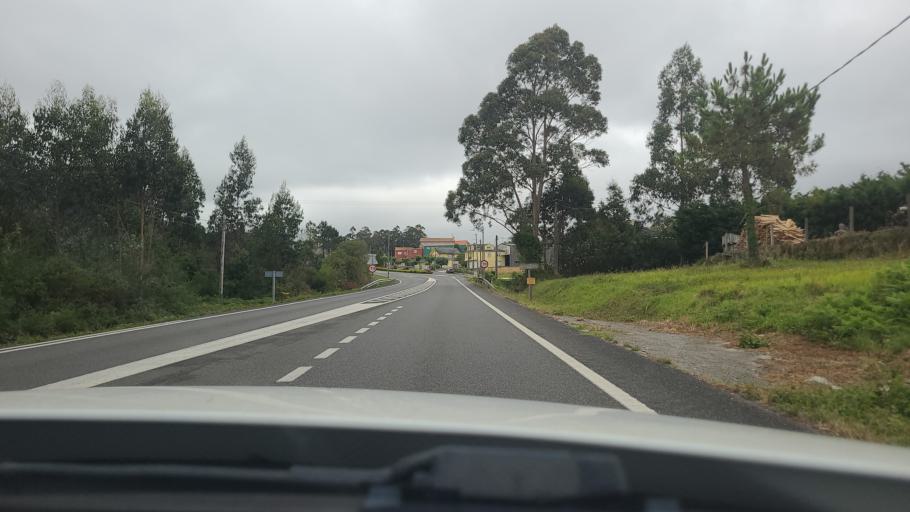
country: ES
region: Galicia
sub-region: Provincia da Coruna
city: Dumbria
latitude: 43.0098
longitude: -9.1608
